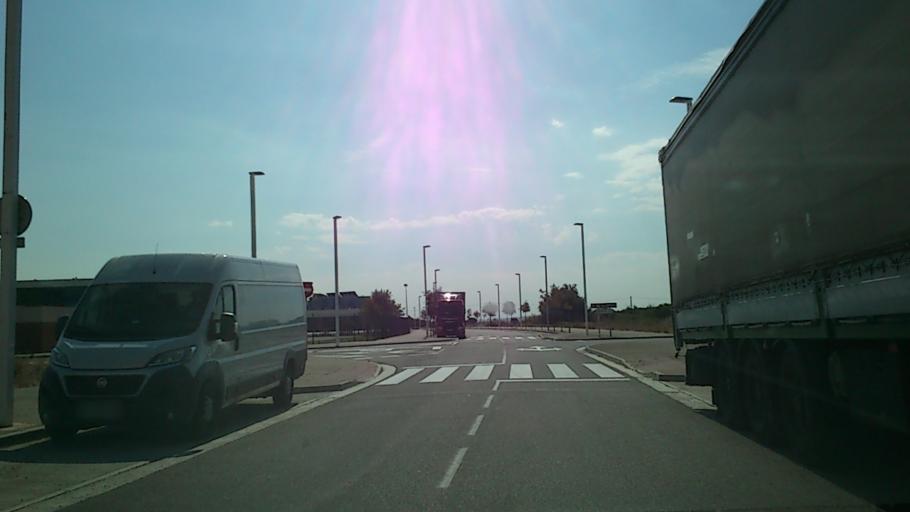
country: ES
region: Aragon
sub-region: Provincia de Zaragoza
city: Puebla de Alfinden
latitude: 41.6323
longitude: -0.7589
